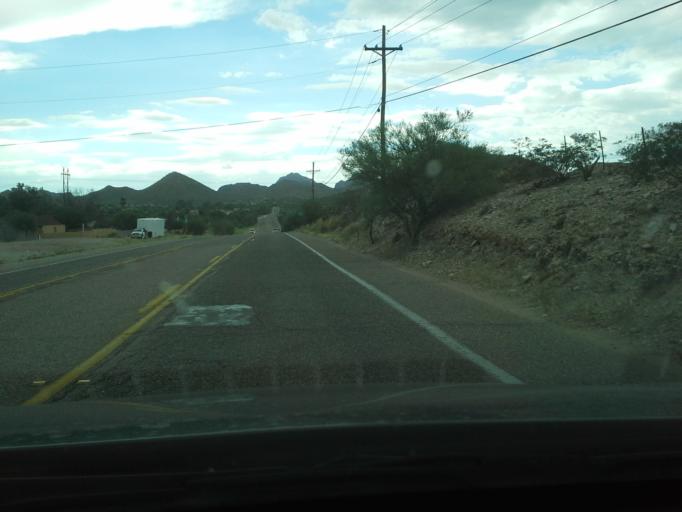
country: US
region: Arizona
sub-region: Pima County
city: South Tucson
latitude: 32.2069
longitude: -111.0135
